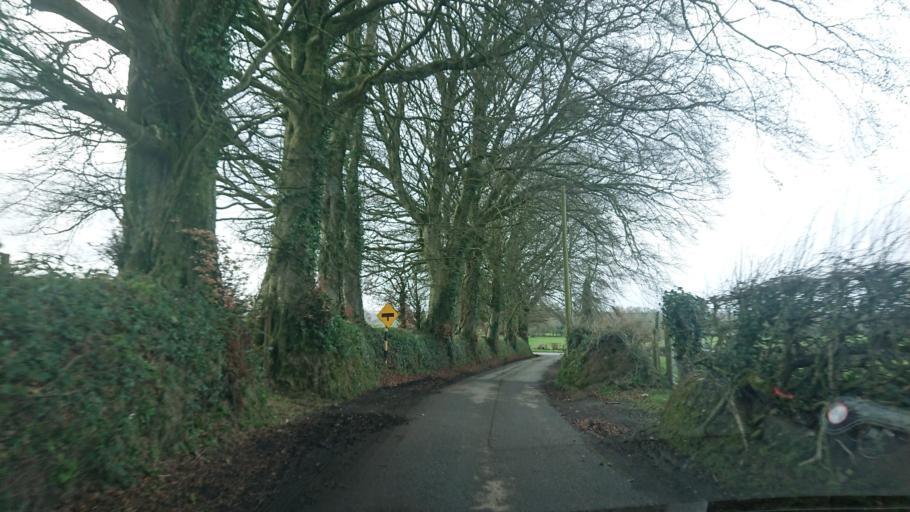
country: IE
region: Leinster
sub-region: Kildare
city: Eadestown
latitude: 53.1602
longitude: -6.5993
